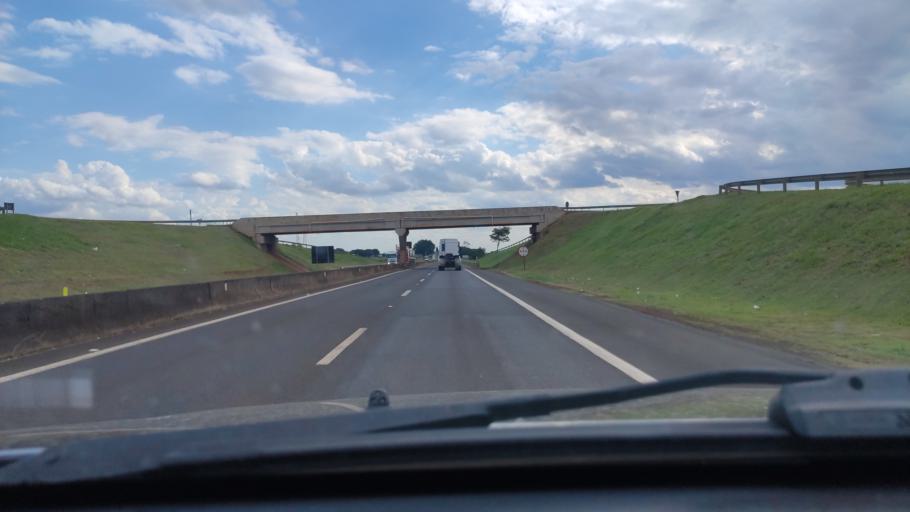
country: BR
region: Sao Paulo
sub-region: Santa Cruz Do Rio Pardo
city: Santa Cruz do Rio Pardo
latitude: -22.8969
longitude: -49.7315
